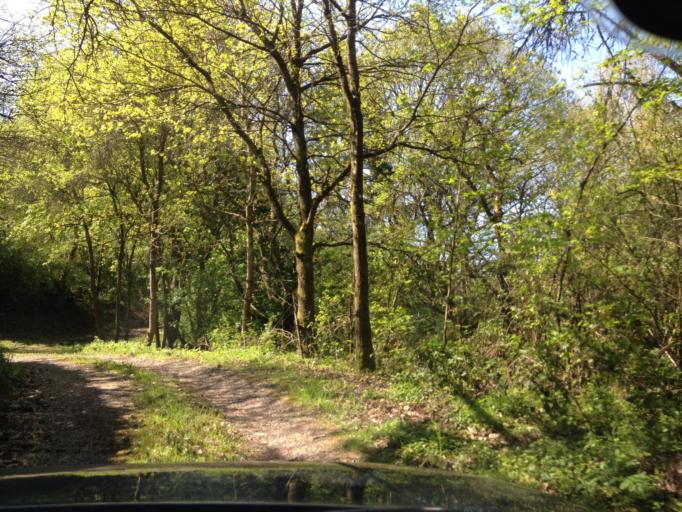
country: DE
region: Saarland
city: Hangard
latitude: 49.3749
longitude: 7.2172
